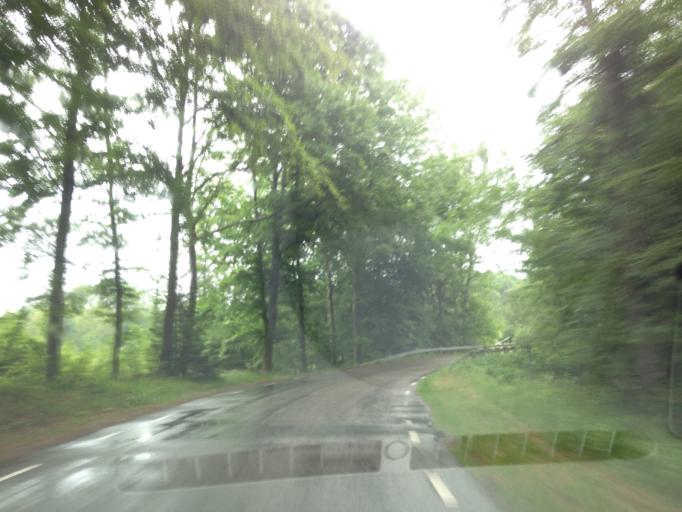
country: SE
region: Vaestra Goetaland
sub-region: Marks Kommun
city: Horred
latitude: 57.1607
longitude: 12.6803
